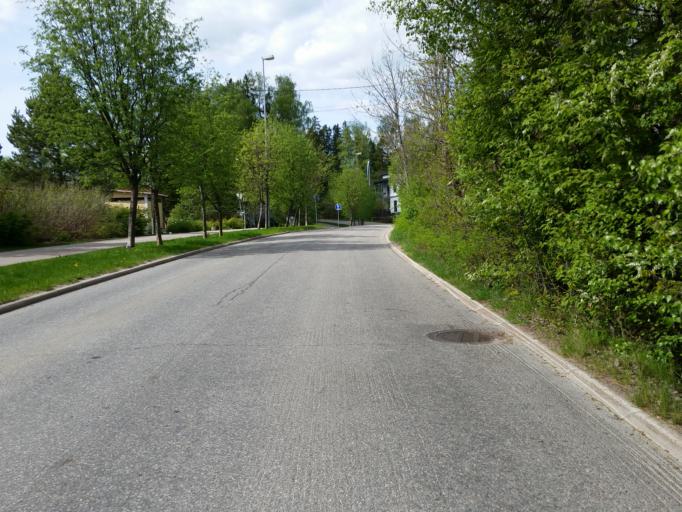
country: FI
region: Uusimaa
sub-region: Helsinki
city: Espoo
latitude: 60.2128
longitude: 24.6399
